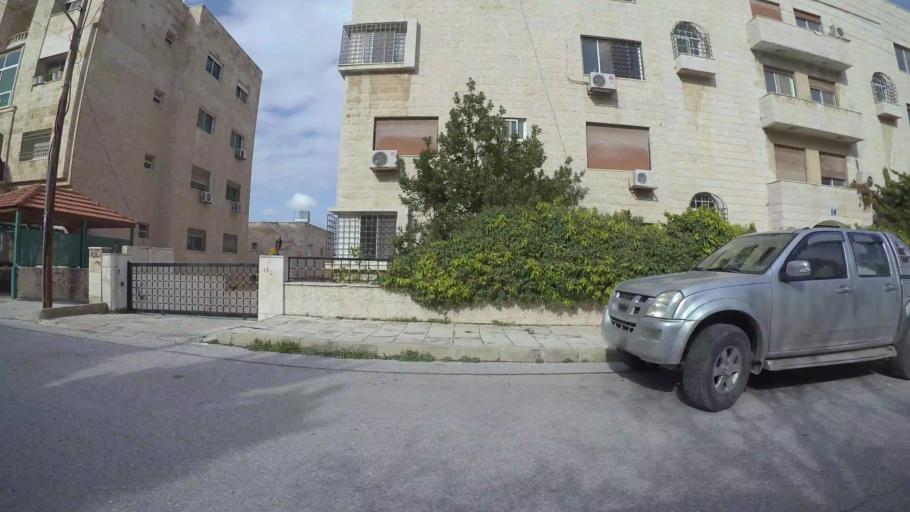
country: JO
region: Amman
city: Al Jubayhah
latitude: 32.0194
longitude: 35.8585
